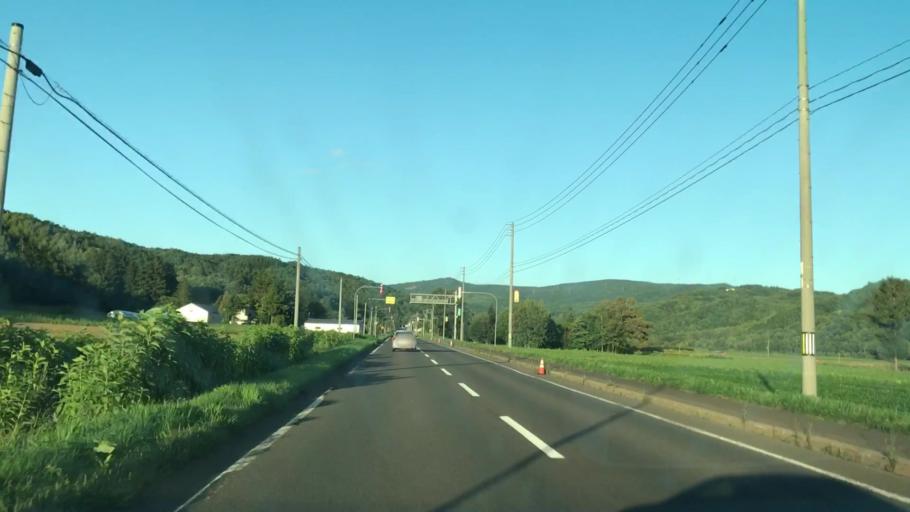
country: JP
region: Hokkaido
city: Niseko Town
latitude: 42.7983
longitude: 140.9604
